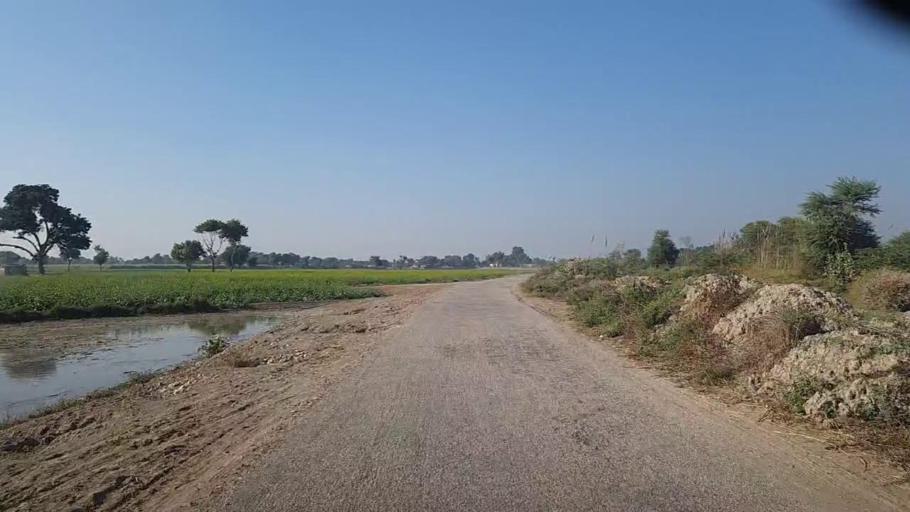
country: PK
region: Sindh
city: Darya Khan Marri
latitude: 26.6905
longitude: 68.3507
